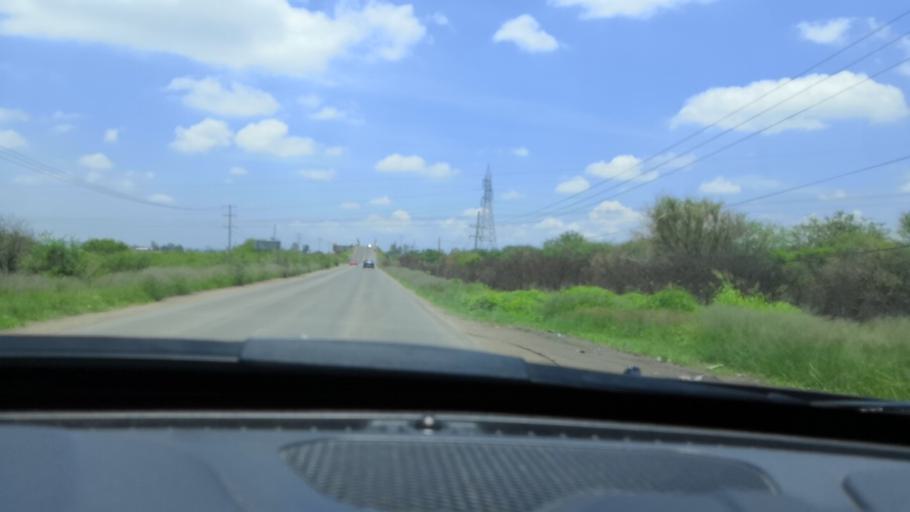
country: MX
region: Guanajuato
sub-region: Silao de la Victoria
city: El Refugio de los Sauces
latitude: 21.0143
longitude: -101.5795
